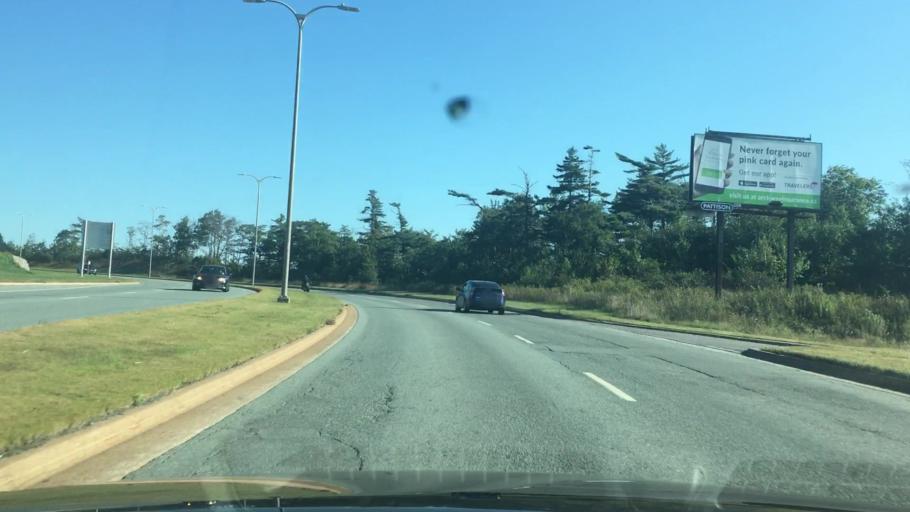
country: CA
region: Nova Scotia
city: Dartmouth
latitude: 44.7184
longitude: -63.5809
